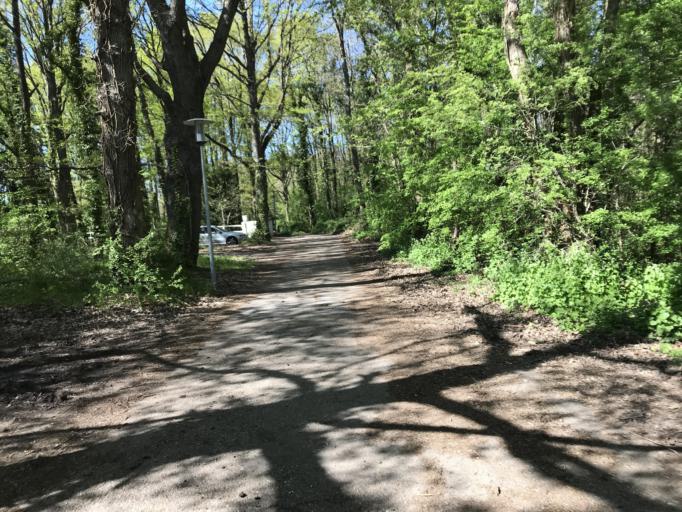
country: FR
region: Ile-de-France
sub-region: Departement de l'Essonne
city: Villejust
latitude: 48.6869
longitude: 2.2384
